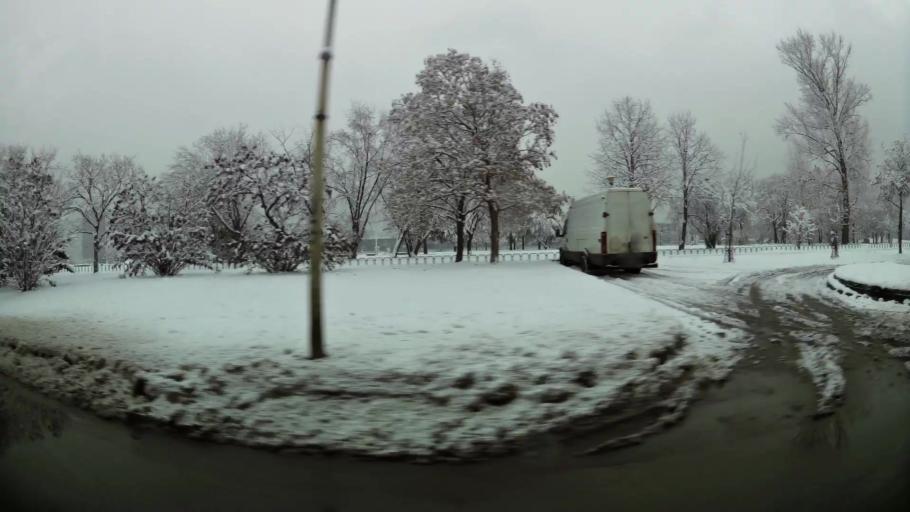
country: RS
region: Central Serbia
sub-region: Belgrade
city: Novi Beograd
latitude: 44.8062
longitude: 20.4407
